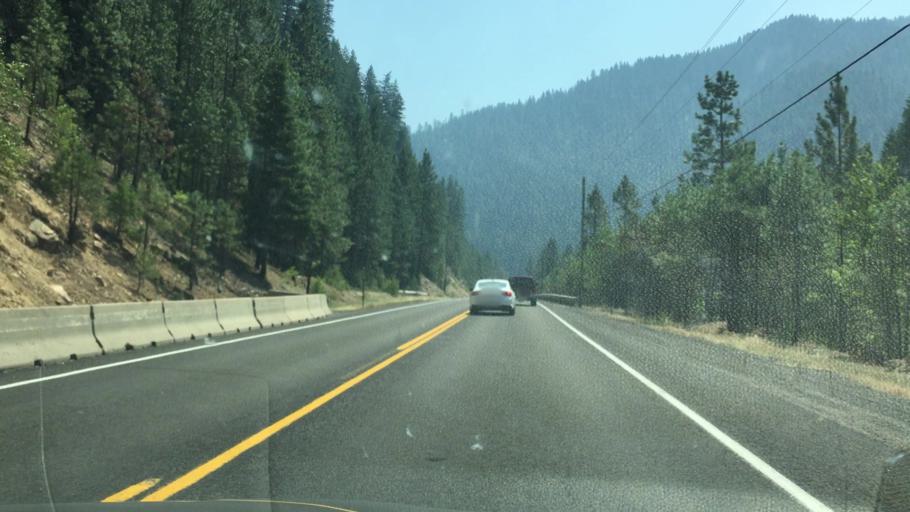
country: US
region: Idaho
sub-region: Valley County
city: McCall
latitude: 45.1565
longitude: -116.2982
